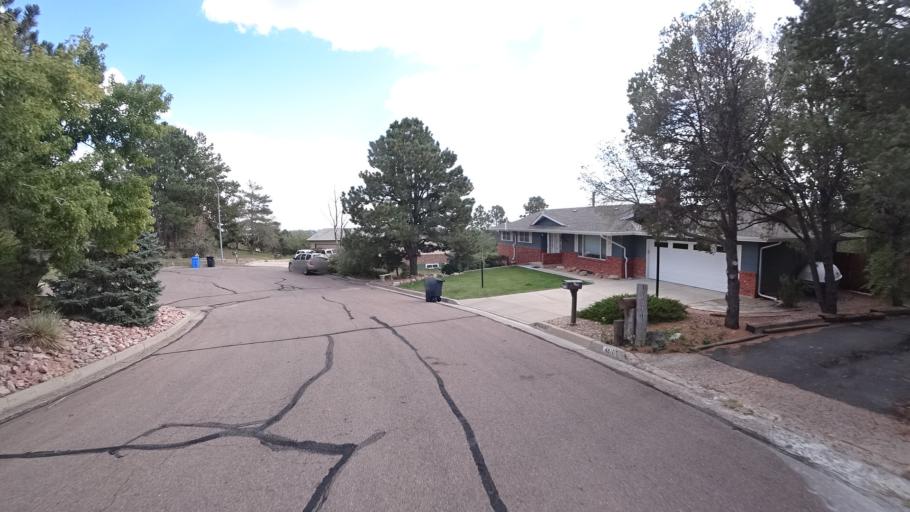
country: US
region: Colorado
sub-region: El Paso County
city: Cimarron Hills
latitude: 38.8686
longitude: -104.7379
